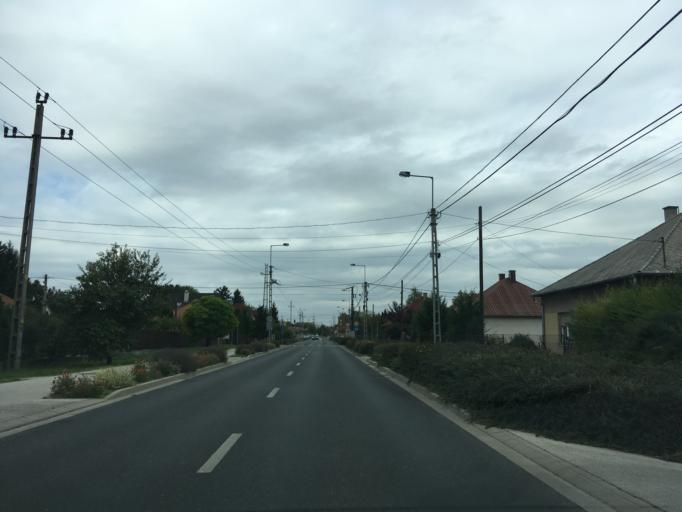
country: HU
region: Pest
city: Szazhalombatta
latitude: 47.3202
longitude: 18.9051
